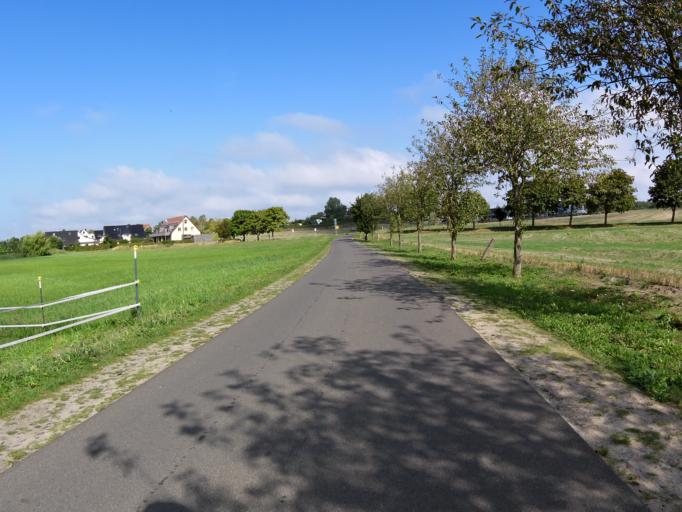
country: DE
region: Mecklenburg-Vorpommern
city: Loddin
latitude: 54.0073
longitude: 14.0472
